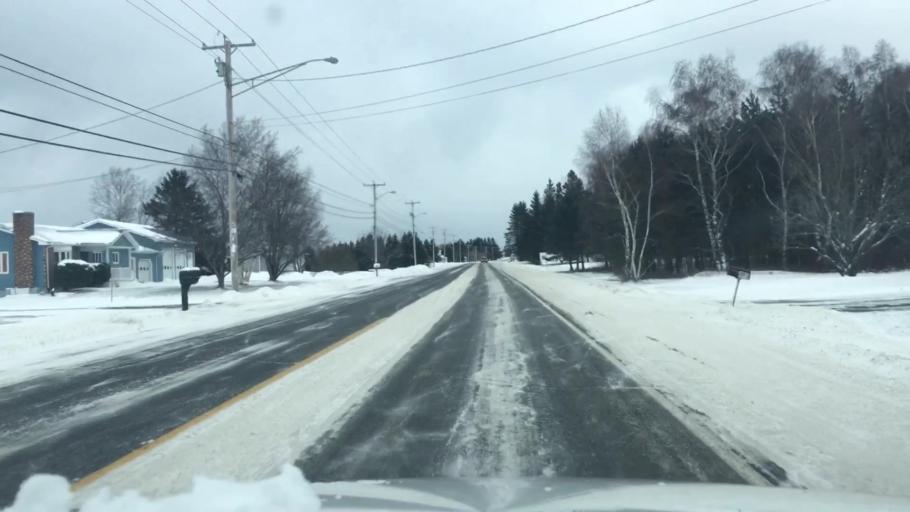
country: US
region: Maine
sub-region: Aroostook County
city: Madawaska
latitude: 47.3456
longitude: -68.2543
